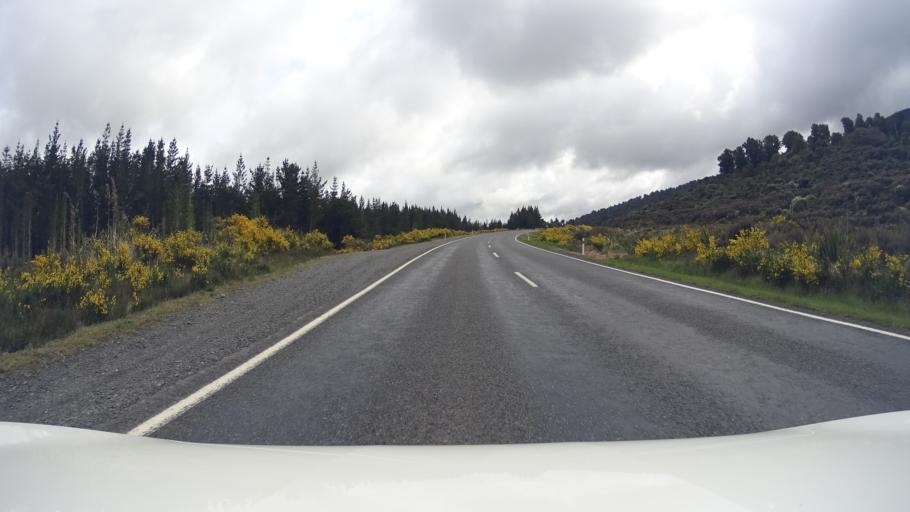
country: NZ
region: Manawatu-Wanganui
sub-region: Ruapehu District
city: Waiouru
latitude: -39.2248
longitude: 175.3970
